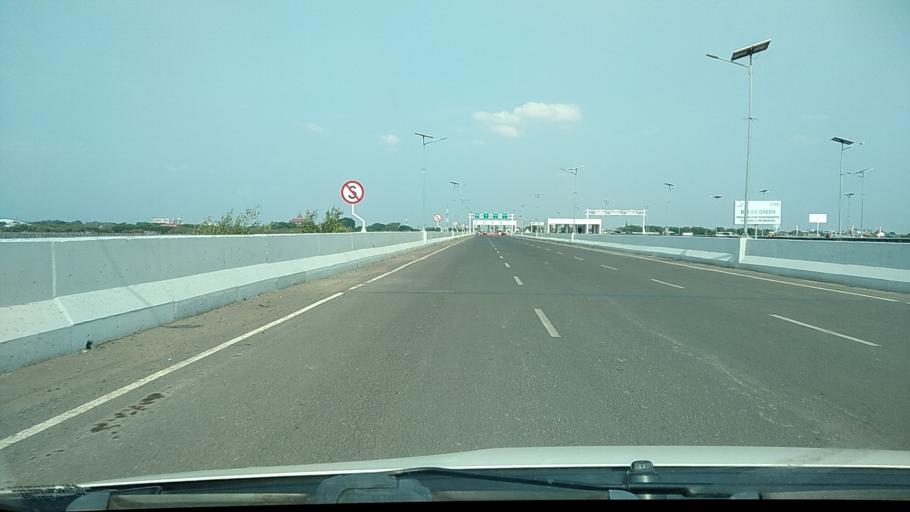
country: ID
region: Central Java
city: Semarang
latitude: -6.9637
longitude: 110.3779
